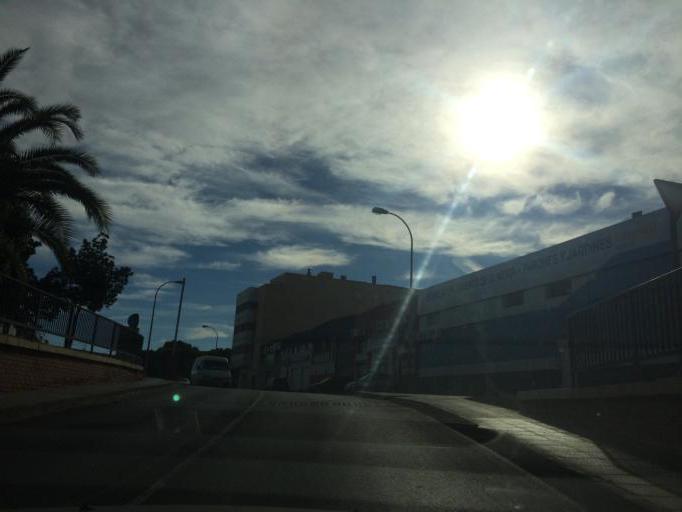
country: ES
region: Andalusia
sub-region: Provincia de Almeria
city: Almeria
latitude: 36.8384
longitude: -2.4431
